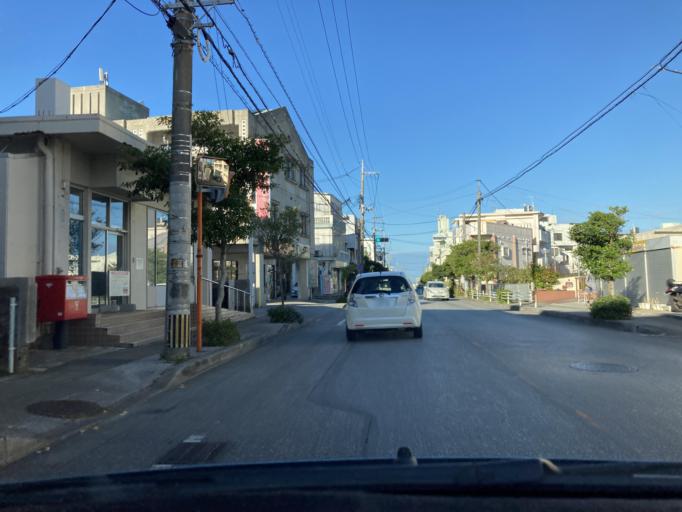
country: JP
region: Okinawa
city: Naha-shi
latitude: 26.2103
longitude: 127.7114
